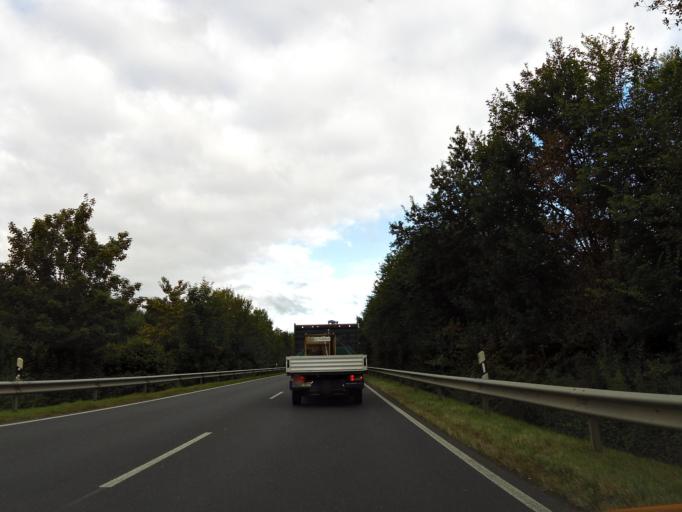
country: DE
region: Lower Saxony
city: Einbeck
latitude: 51.8161
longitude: 9.8368
